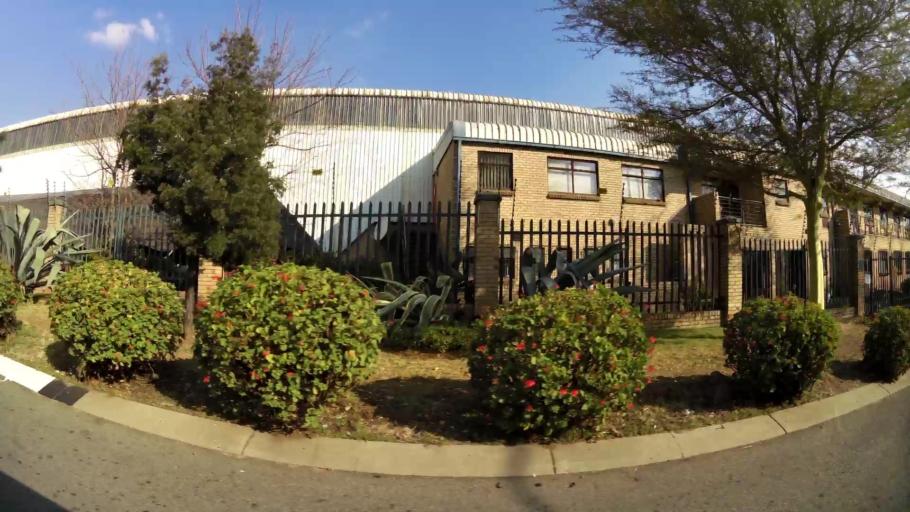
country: ZA
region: Gauteng
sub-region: City of Johannesburg Metropolitan Municipality
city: Modderfontein
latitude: -26.1073
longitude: 28.1748
